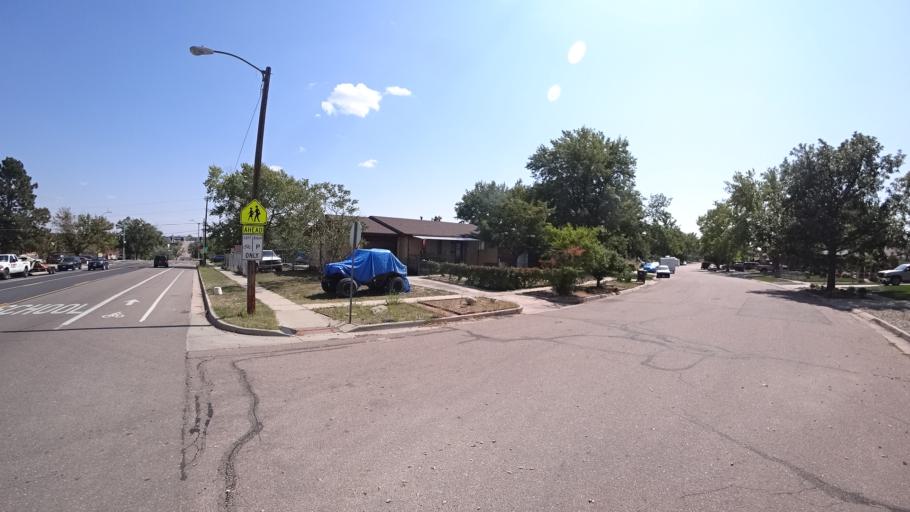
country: US
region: Colorado
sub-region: El Paso County
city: Colorado Springs
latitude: 38.8357
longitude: -104.7680
